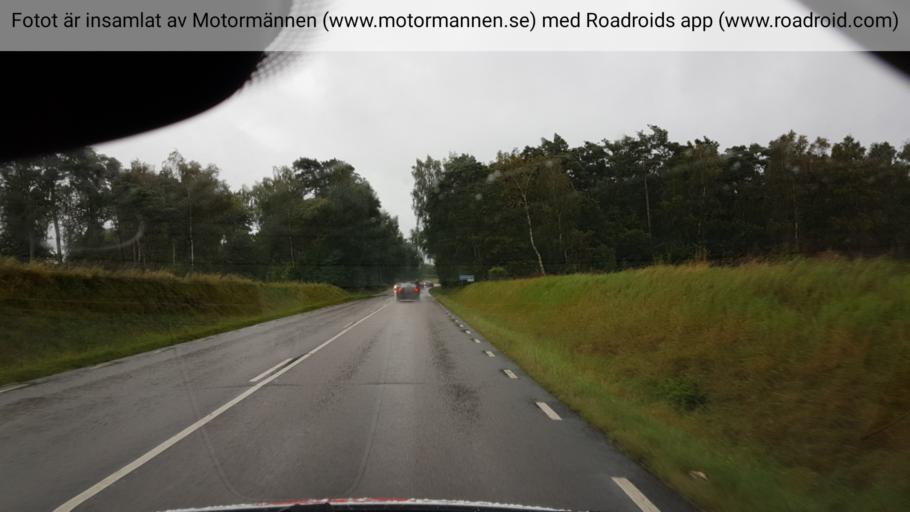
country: SE
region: Halland
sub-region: Laholms Kommun
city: Laholm
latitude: 56.4829
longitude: 13.0409
